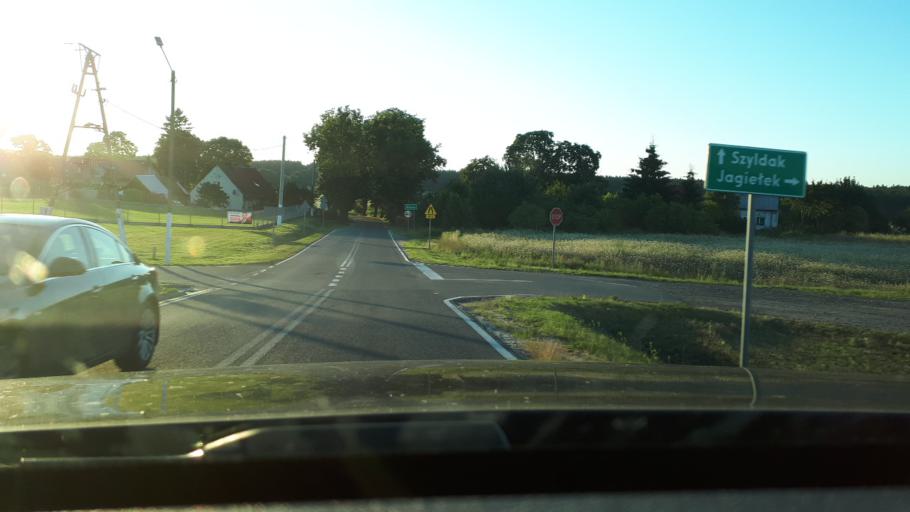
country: PL
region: Warmian-Masurian Voivodeship
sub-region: Powiat olsztynski
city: Olsztynek
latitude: 53.6001
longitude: 20.2730
